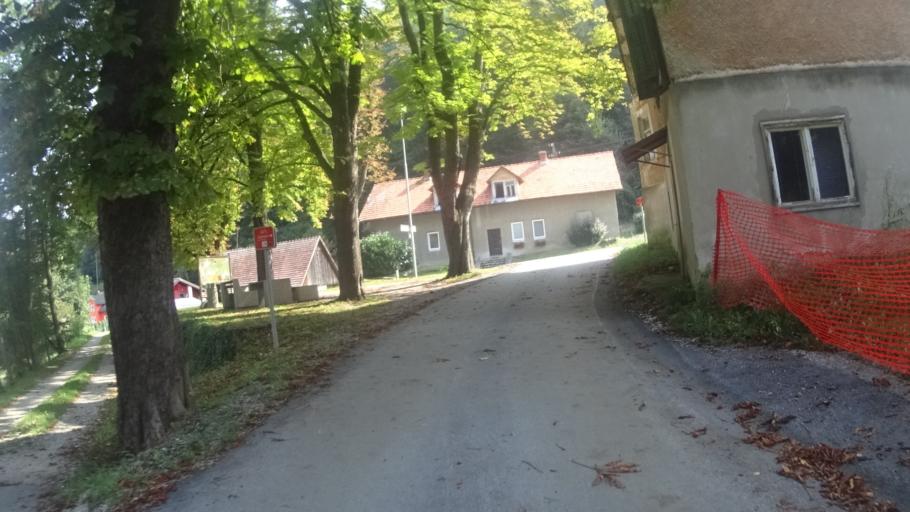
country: SI
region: Selnica ob Dravi
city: Selnica ob Dravi
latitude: 46.5568
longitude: 15.4585
